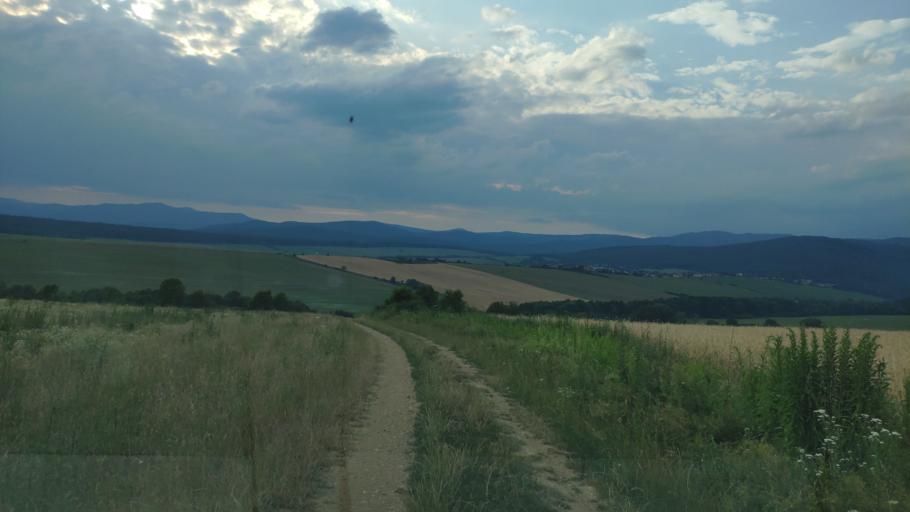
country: SK
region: Kosicky
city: Moldava nad Bodvou
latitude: 48.6969
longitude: 20.9909
